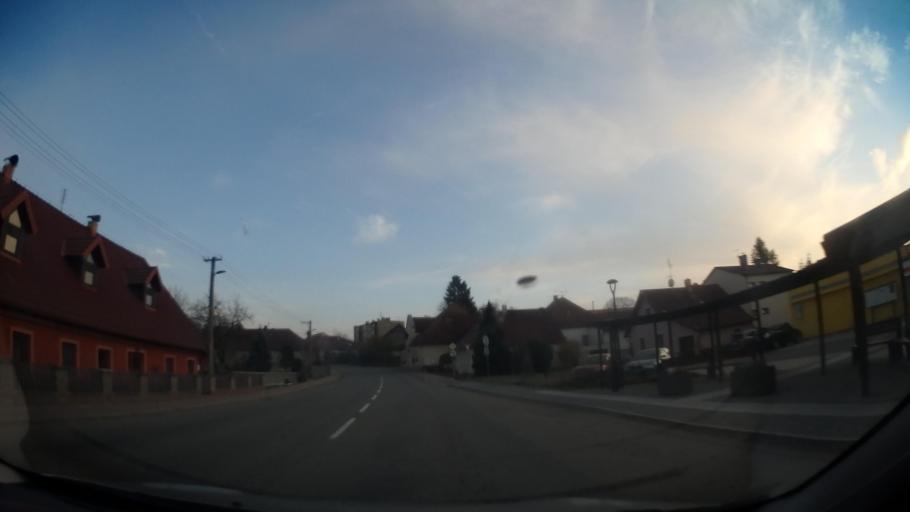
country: CZ
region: Central Bohemia
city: Cechtice
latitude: 49.5579
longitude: 15.1163
